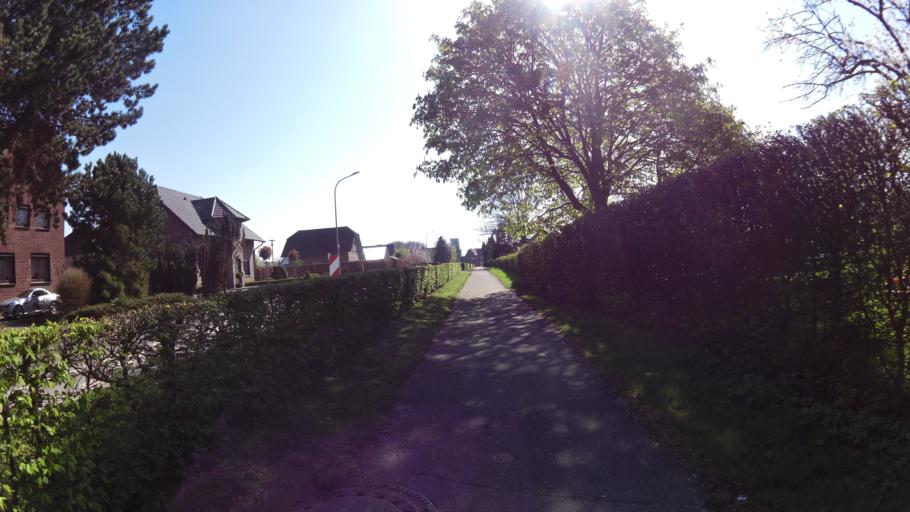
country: DE
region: North Rhine-Westphalia
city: Geilenkirchen
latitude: 50.9538
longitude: 6.1645
